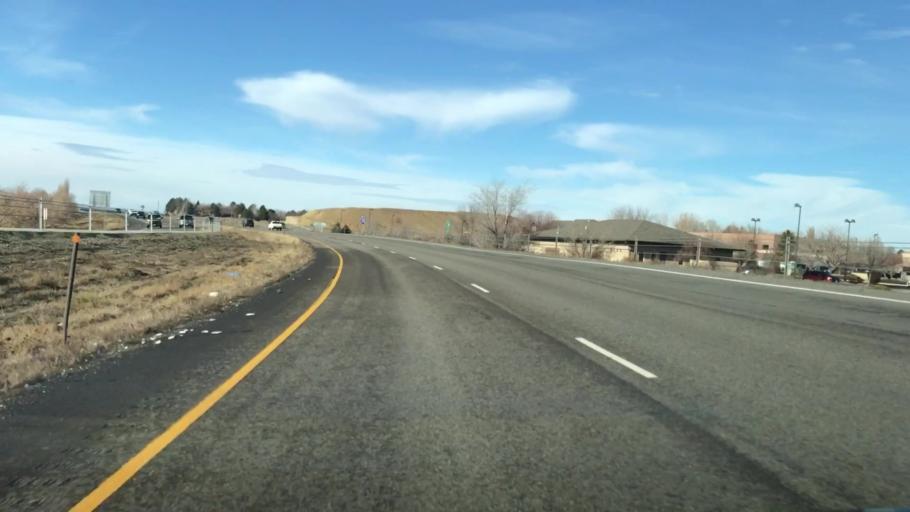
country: US
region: Colorado
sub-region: Mesa County
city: Grand Junction
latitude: 39.1154
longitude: -108.5439
